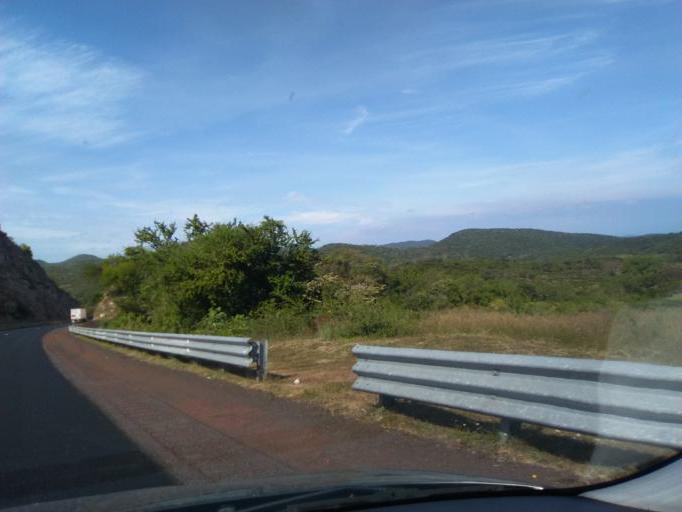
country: MX
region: Guerrero
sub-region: Huitzuco de los Figueroa
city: Ciudad de Huitzuco
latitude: 18.2223
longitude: -99.2173
